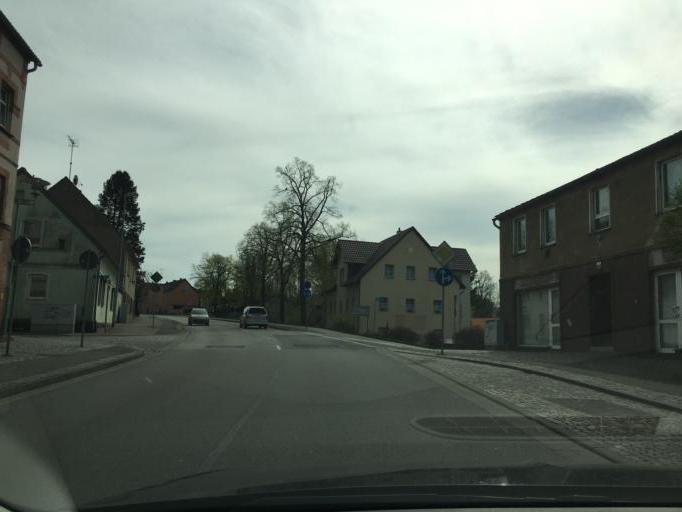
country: DE
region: Brandenburg
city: Spremberg
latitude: 51.5675
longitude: 14.3870
